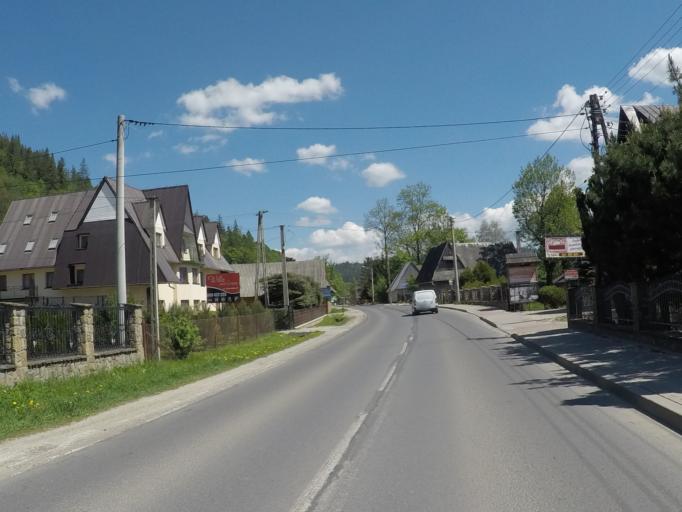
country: PL
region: Lesser Poland Voivodeship
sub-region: Powiat tatrzanski
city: Poronin
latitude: 49.3314
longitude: 20.0205
